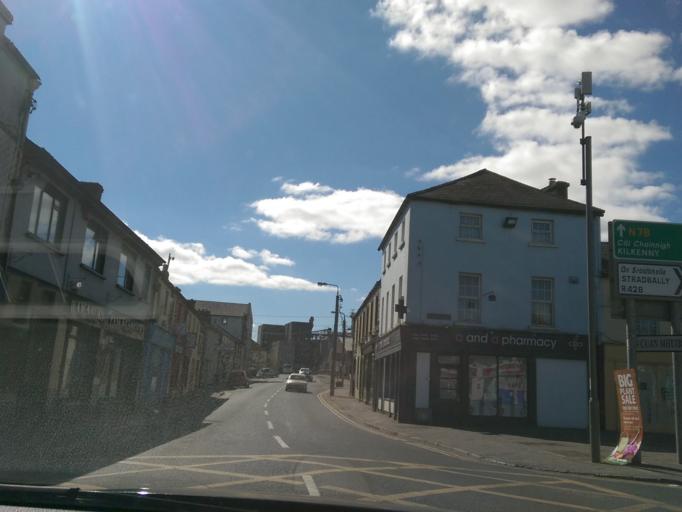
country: IE
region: Leinster
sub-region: Kildare
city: Athy
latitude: 52.9913
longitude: -6.9889
